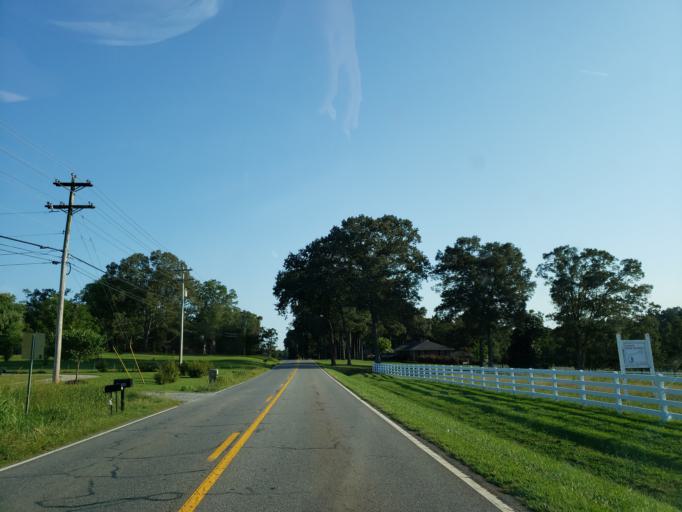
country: US
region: Georgia
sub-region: Murray County
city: Chatsworth
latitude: 34.7786
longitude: -84.8243
